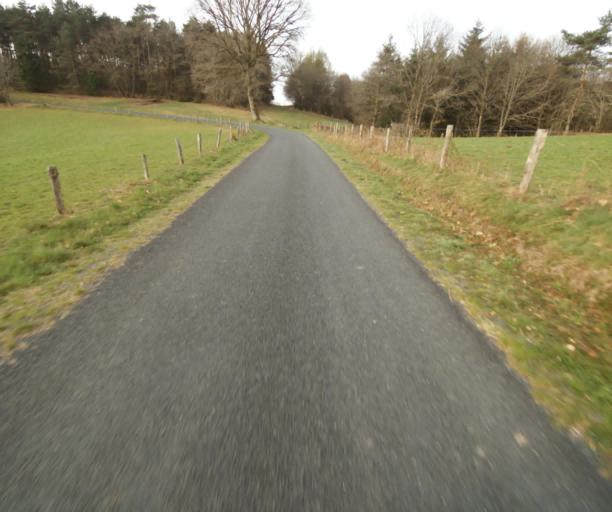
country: FR
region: Limousin
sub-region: Departement de la Correze
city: Treignac
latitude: 45.4534
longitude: 1.8092
